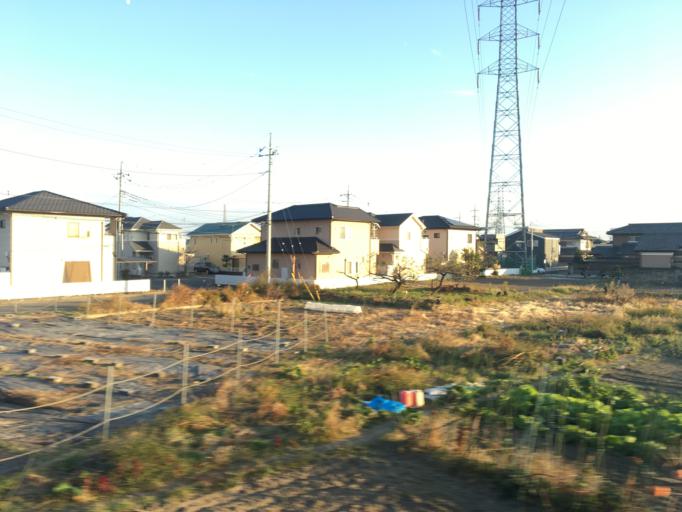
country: JP
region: Gunma
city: Maebashi-shi
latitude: 36.3720
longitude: 139.0378
